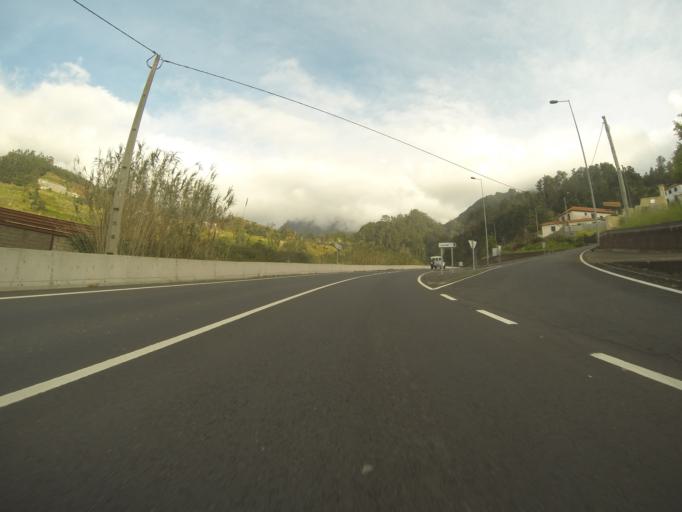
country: PT
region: Madeira
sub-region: Sao Vicente
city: Sao Vicente
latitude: 32.7745
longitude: -17.0315
